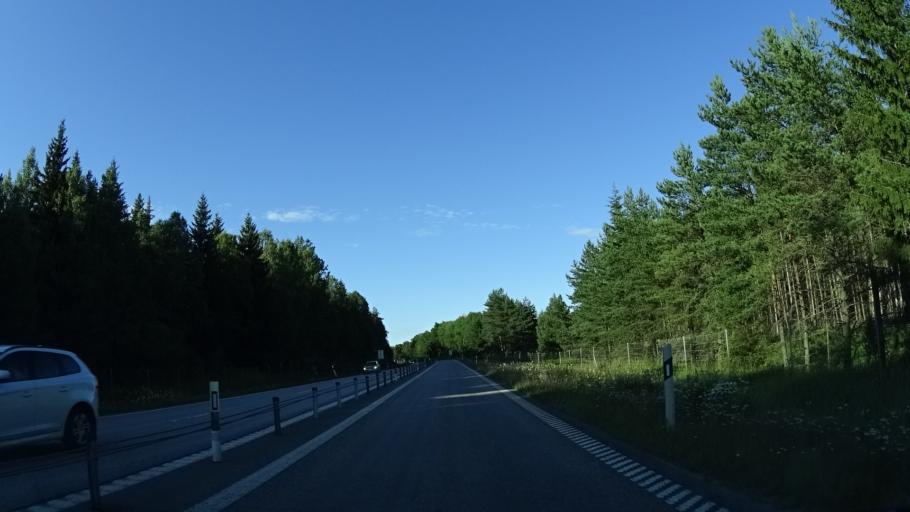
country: SE
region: Stockholm
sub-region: Vallentuna Kommun
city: Vallentuna
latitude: 59.5235
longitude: 18.1858
